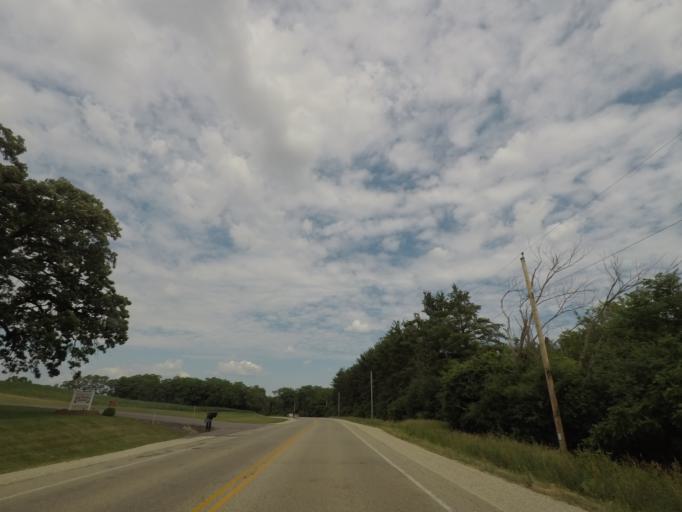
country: US
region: Wisconsin
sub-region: Rock County
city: Milton
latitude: 42.8229
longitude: -88.9183
